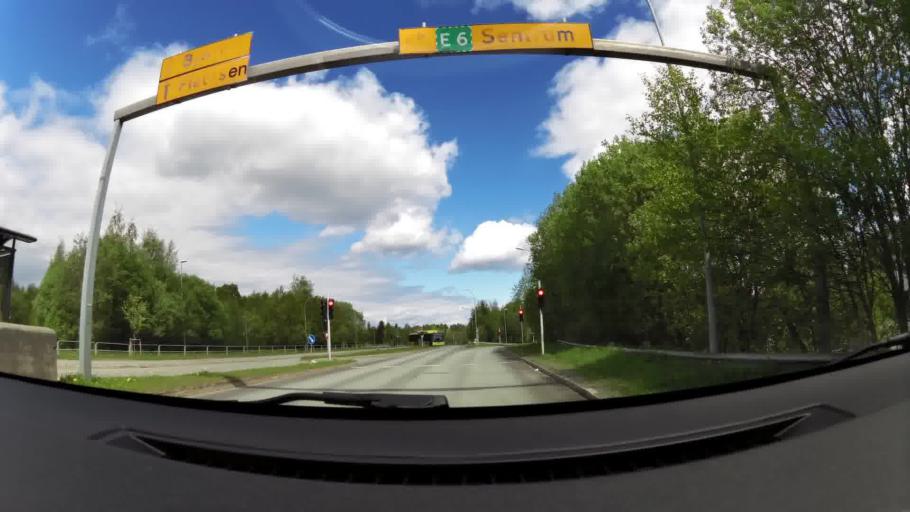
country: NO
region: Sor-Trondelag
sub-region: Trondheim
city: Trondheim
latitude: 63.3689
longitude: 10.3453
